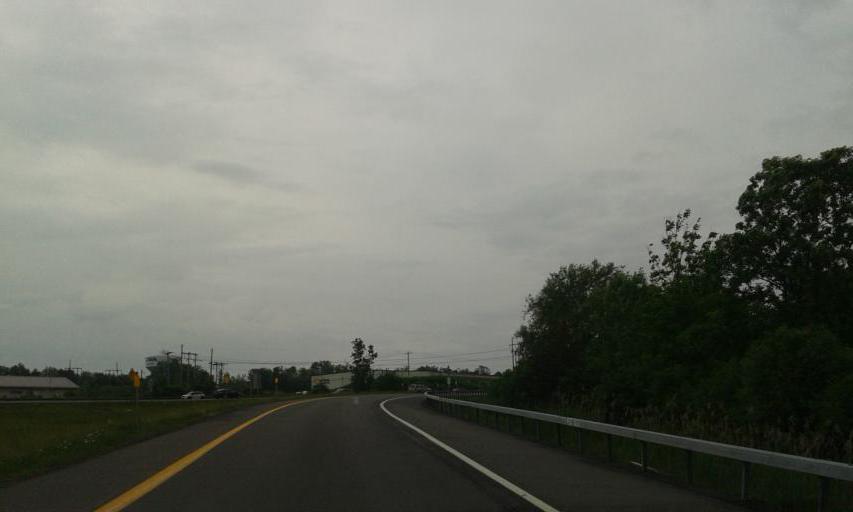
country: US
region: New York
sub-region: Onondaga County
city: Seneca Knolls
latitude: 43.1138
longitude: -76.2730
